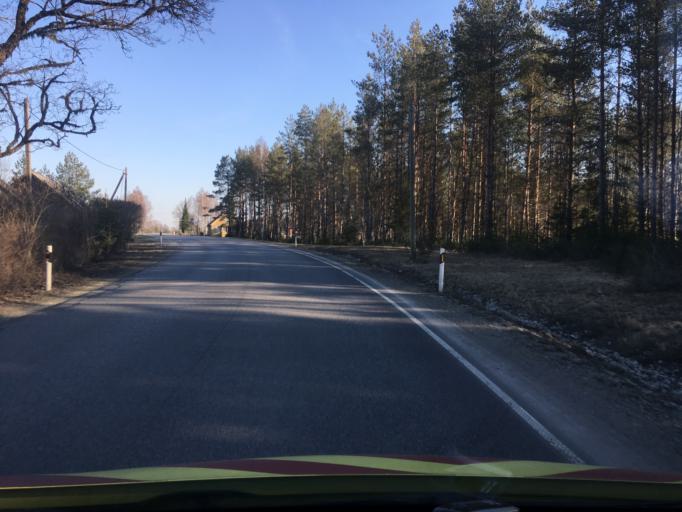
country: EE
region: Raplamaa
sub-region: Rapla vald
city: Rapla
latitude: 59.0123
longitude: 24.8374
